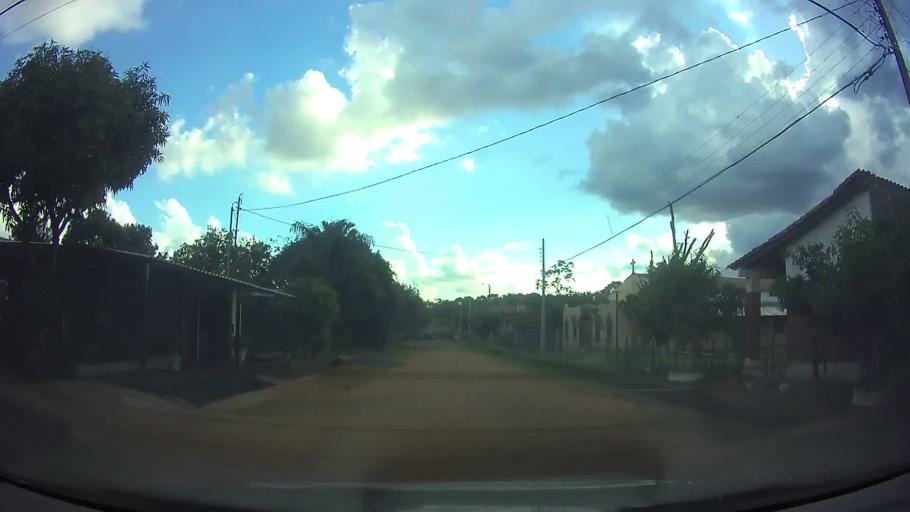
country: PY
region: Central
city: Limpio
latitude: -25.2529
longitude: -57.4596
